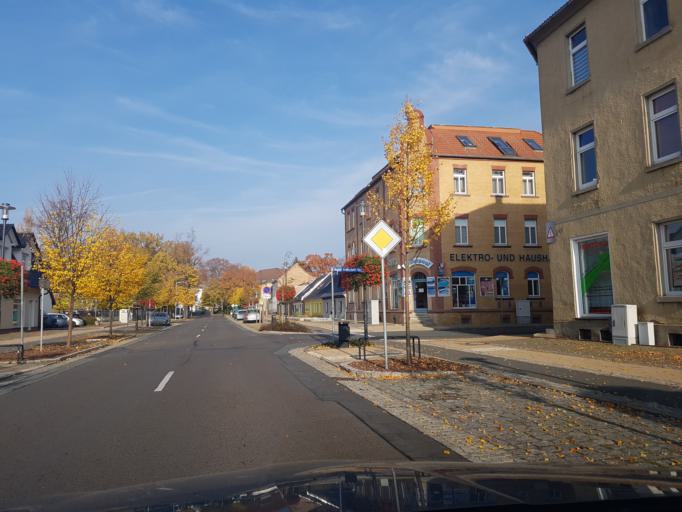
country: DE
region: Brandenburg
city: Elsterwerda
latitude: 51.4611
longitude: 13.5211
